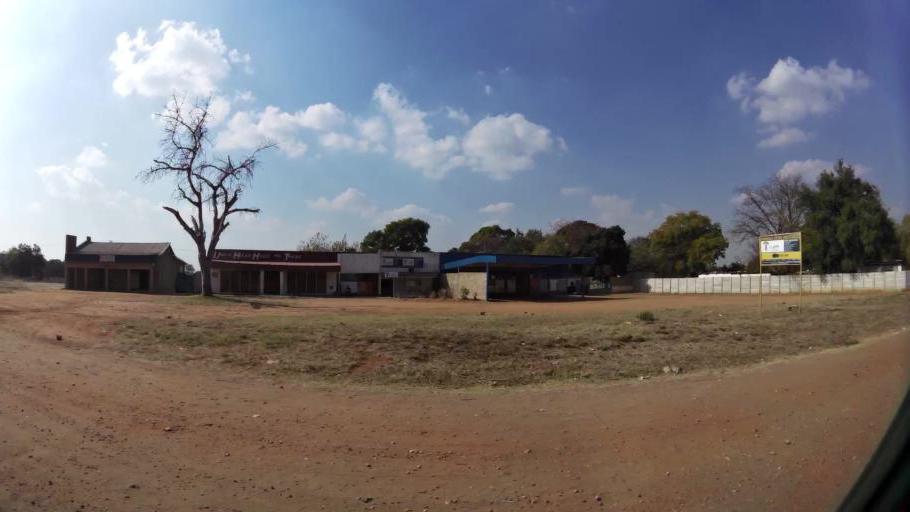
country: ZA
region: North-West
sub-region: Bojanala Platinum District Municipality
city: Rustenburg
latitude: -25.4937
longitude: 27.0861
